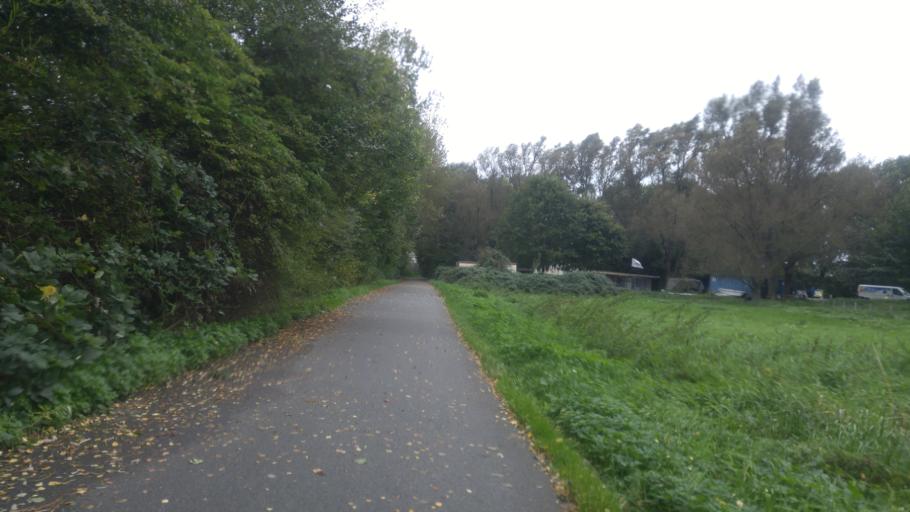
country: DE
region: Bremen
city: Bremen
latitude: 53.1113
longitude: 8.8234
